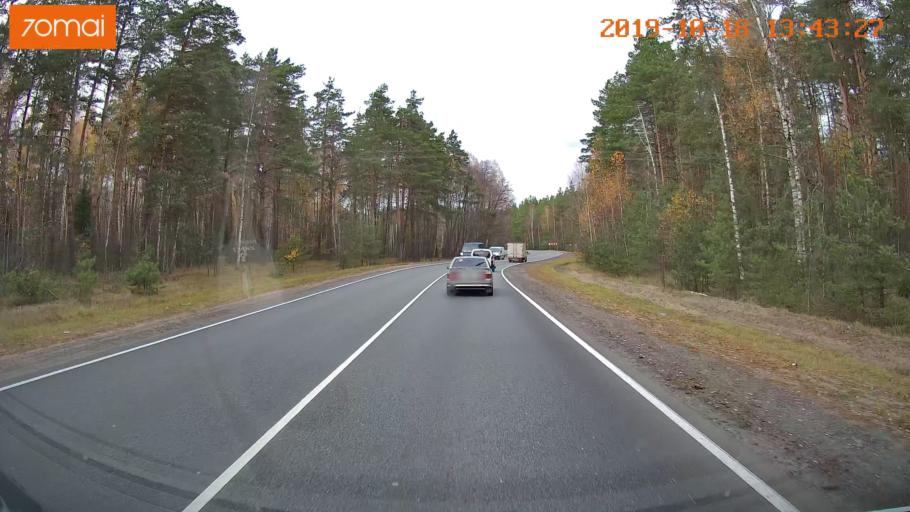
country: RU
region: Rjazan
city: Solotcha
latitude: 54.9305
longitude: 39.9748
